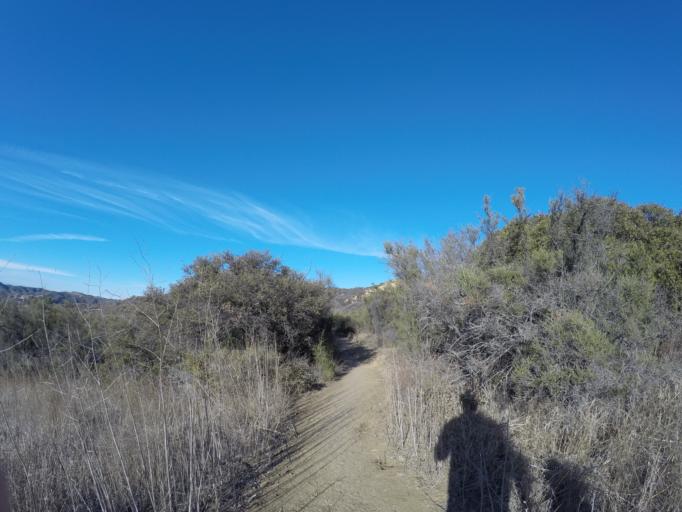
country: US
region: California
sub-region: Los Angeles County
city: Topanga
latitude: 34.1056
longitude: -118.5807
